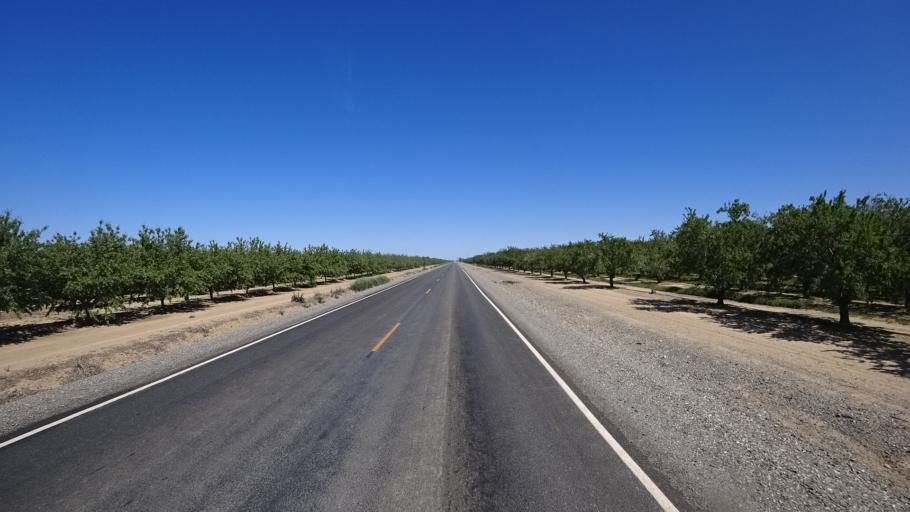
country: US
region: California
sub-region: Glenn County
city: Willows
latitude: 39.6252
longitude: -122.1414
